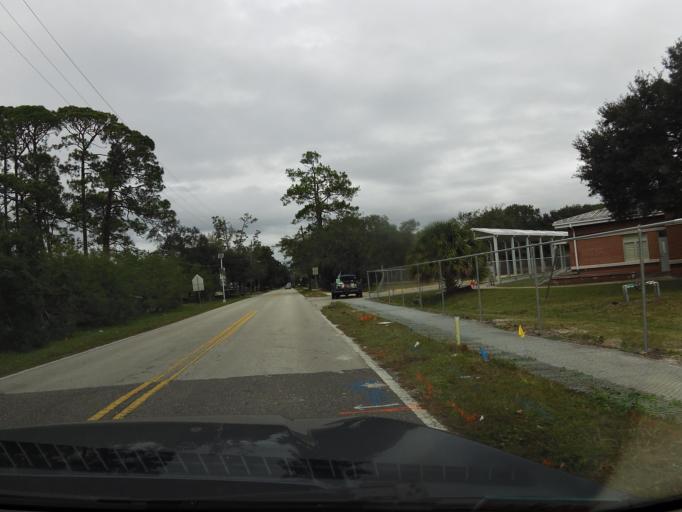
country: US
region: Florida
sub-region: Duval County
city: Jacksonville
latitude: 30.3018
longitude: -81.6030
